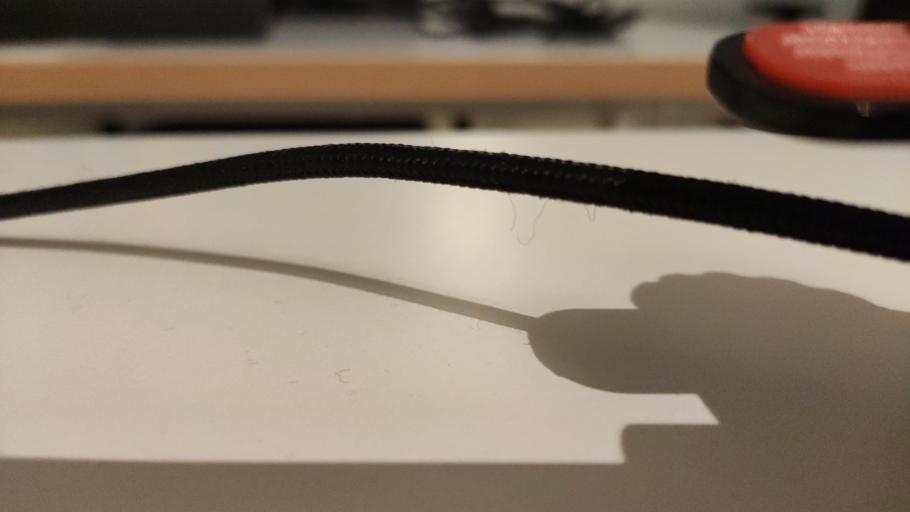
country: RU
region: Moskovskaya
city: Novosin'kovo
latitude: 56.3960
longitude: 37.2730
